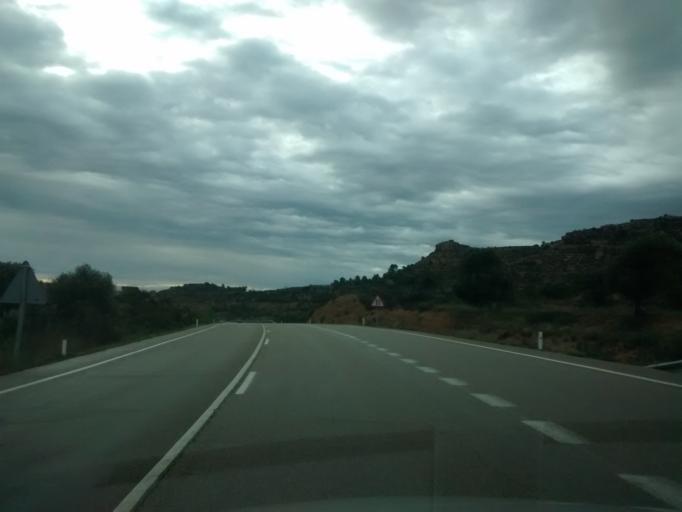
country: ES
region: Aragon
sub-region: Provincia de Zaragoza
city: Maella
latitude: 41.1112
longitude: 0.1684
